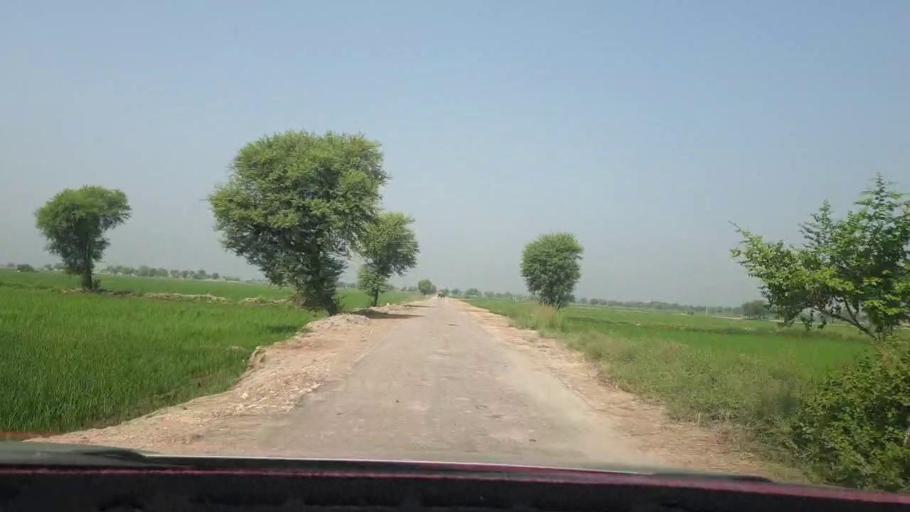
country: PK
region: Sindh
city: Warah
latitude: 27.4308
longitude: 67.8585
